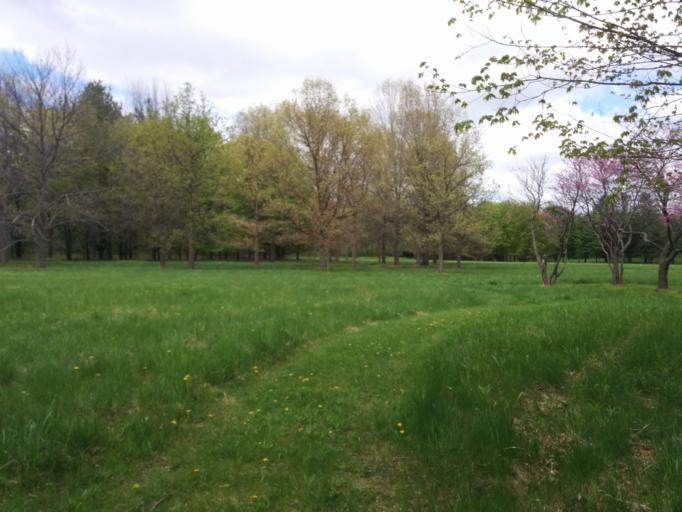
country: US
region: Michigan
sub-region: Midland County
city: Midland
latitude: 43.6022
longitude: -84.2895
